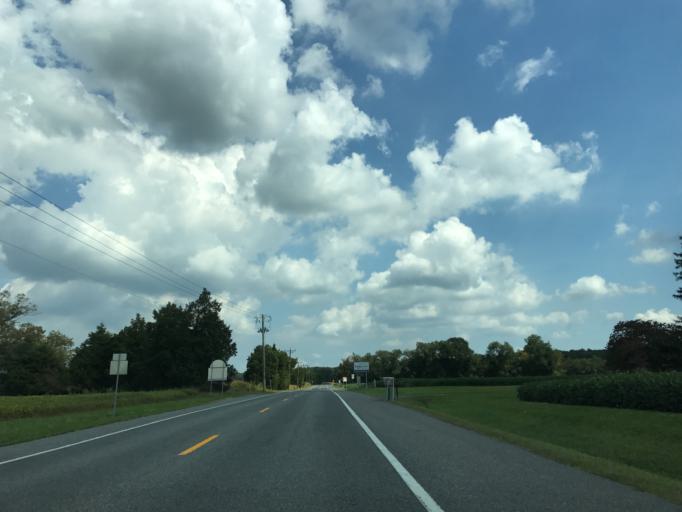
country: US
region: Maryland
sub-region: Caroline County
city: Greensboro
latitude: 39.1429
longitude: -75.7486
